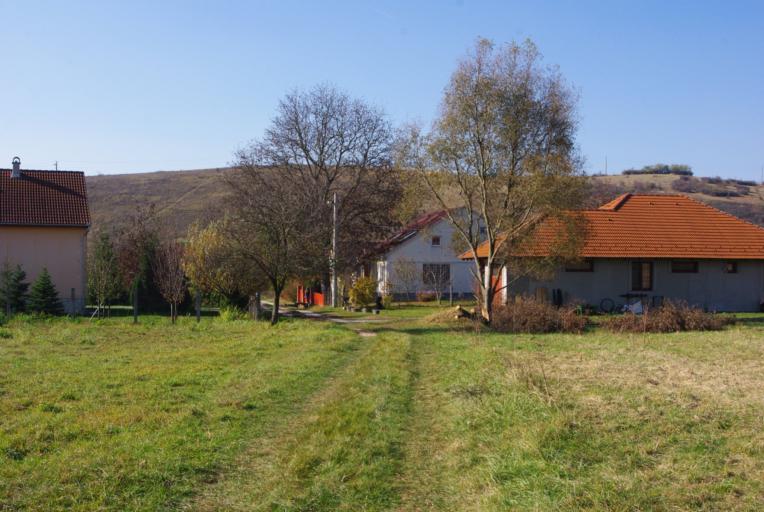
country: HU
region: Borsod-Abauj-Zemplen
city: Borsodnadasd
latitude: 48.0487
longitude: 20.2725
